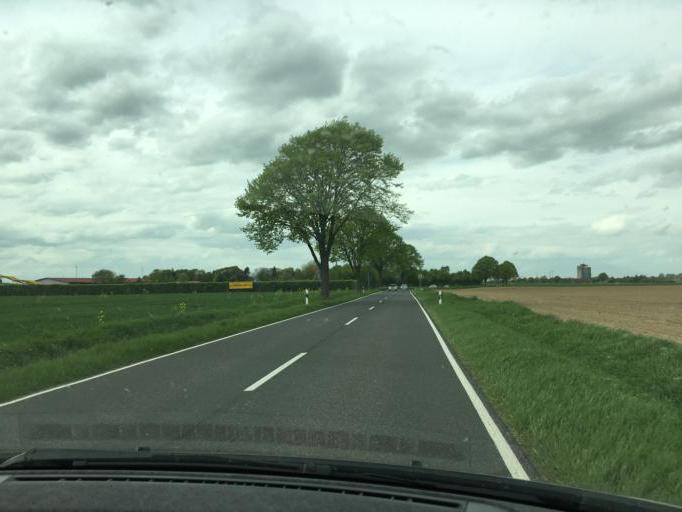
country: DE
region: North Rhine-Westphalia
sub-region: Regierungsbezirk Koln
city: Vettweiss
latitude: 50.7675
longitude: 6.5568
